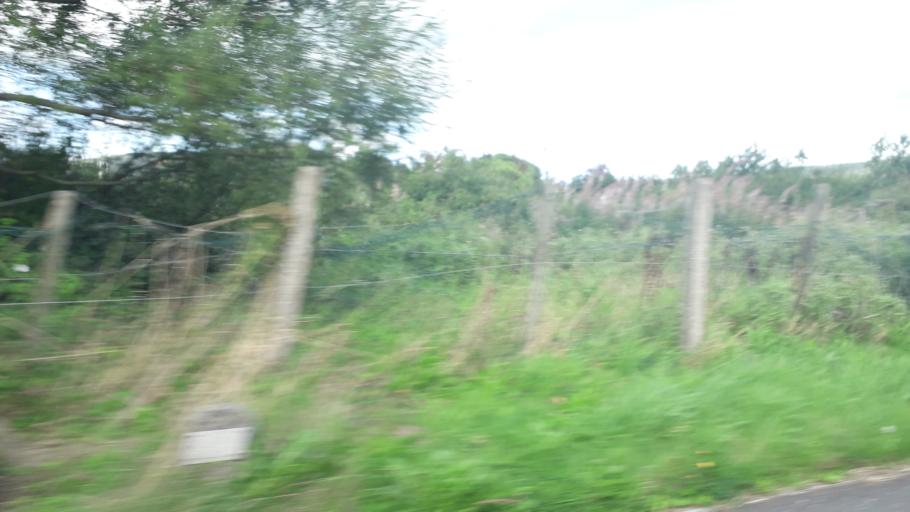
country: IE
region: Leinster
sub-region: Lu
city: Blackrock
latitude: 54.0147
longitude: -6.3163
